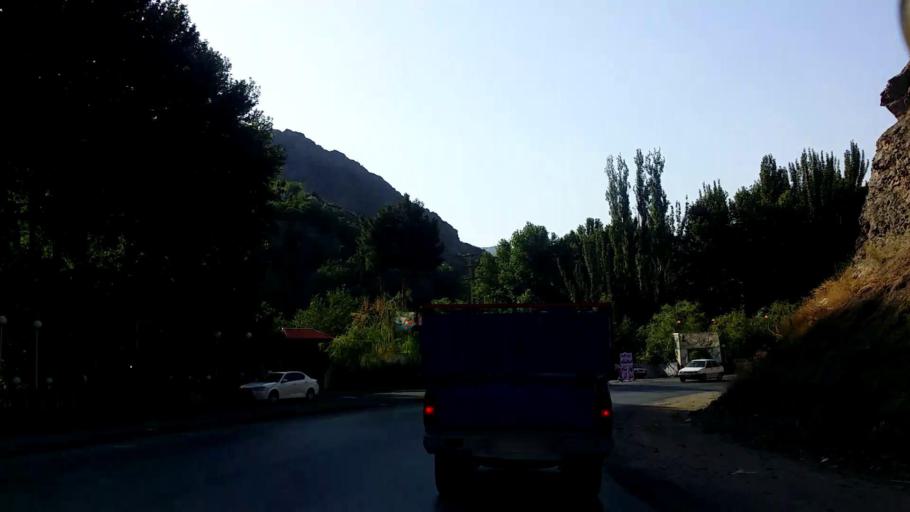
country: IR
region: Alborz
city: Karaj
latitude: 35.8739
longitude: 51.0472
